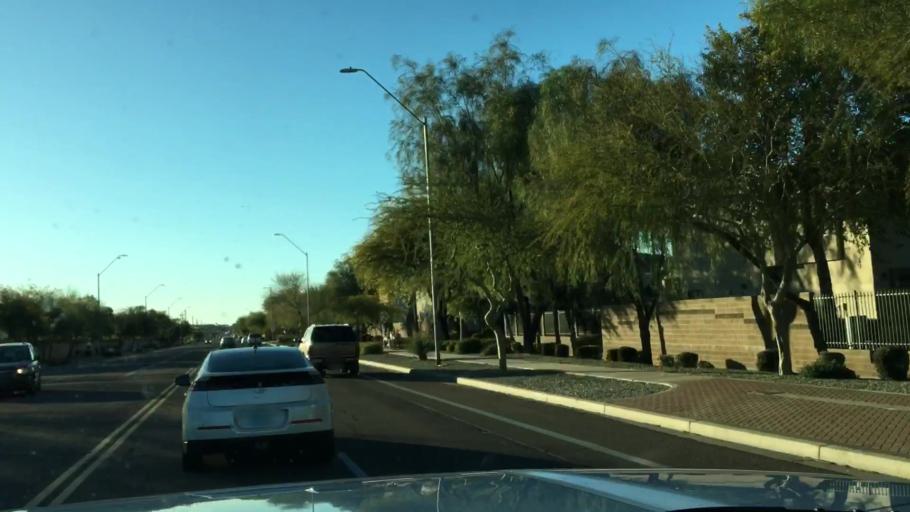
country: US
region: Arizona
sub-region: Maricopa County
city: Paradise Valley
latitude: 33.6699
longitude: -112.0143
